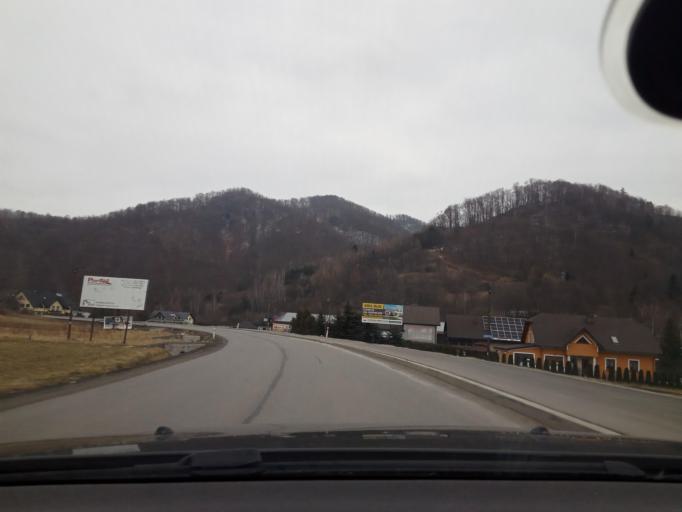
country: PL
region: Lesser Poland Voivodeship
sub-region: Powiat nowosadecki
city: Lacko
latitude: 49.5163
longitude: 20.4153
